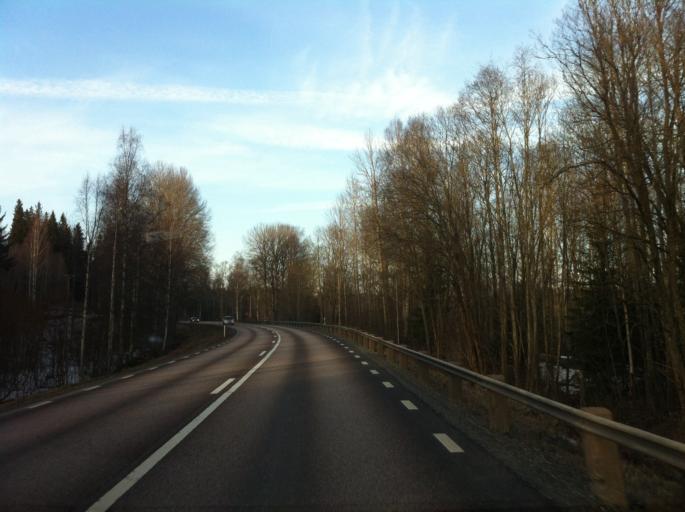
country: SE
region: Vaermland
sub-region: Filipstads Kommun
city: Lesjofors
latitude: 59.8609
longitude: 14.2672
